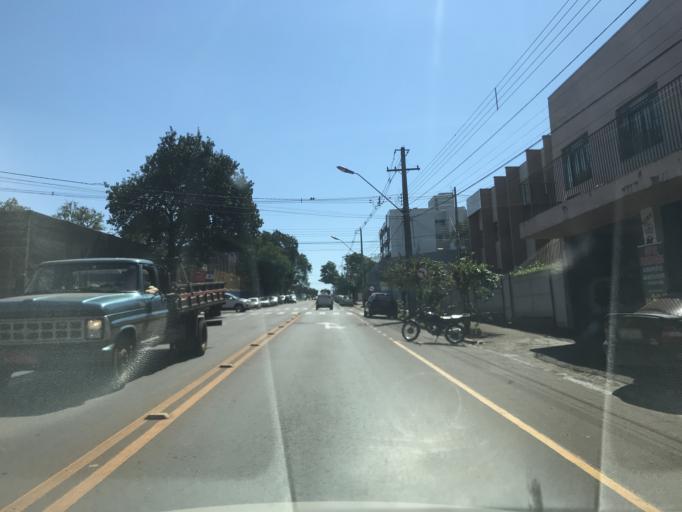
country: BR
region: Parana
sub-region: Toledo
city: Toledo
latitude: -24.7337
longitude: -53.7361
